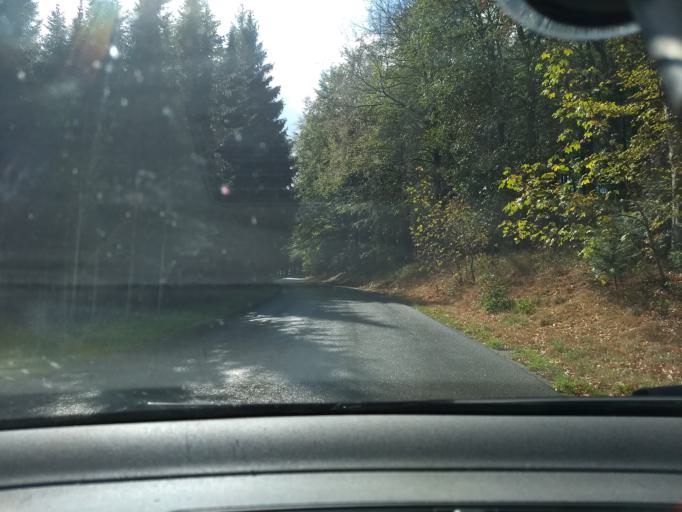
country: DE
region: North Rhine-Westphalia
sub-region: Regierungsbezirk Arnsberg
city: Finnentrop
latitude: 51.2131
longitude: 8.0100
